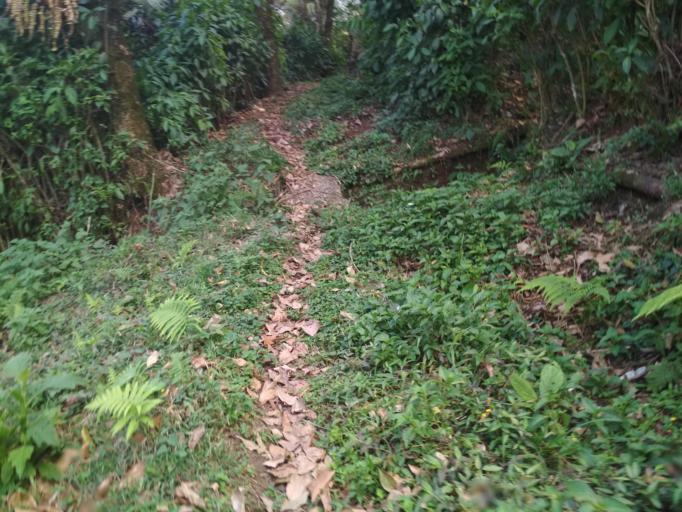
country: MX
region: Veracruz
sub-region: Tlilapan
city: Tonalixco
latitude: 18.7840
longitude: -97.0854
